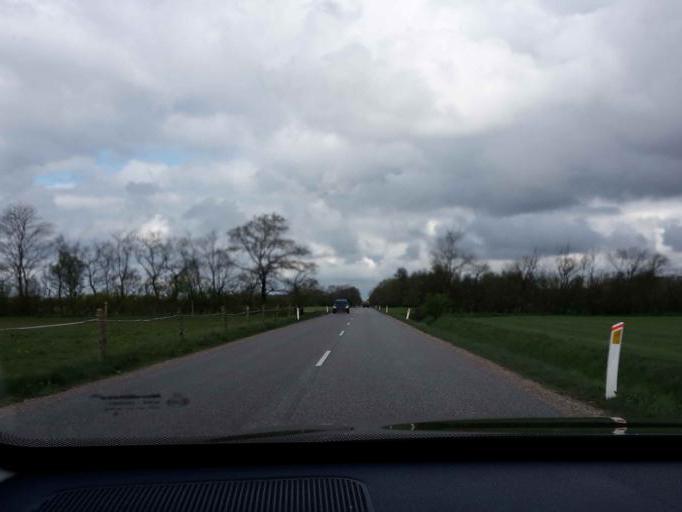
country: DK
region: South Denmark
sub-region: Billund Kommune
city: Grindsted
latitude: 55.7790
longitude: 8.8381
